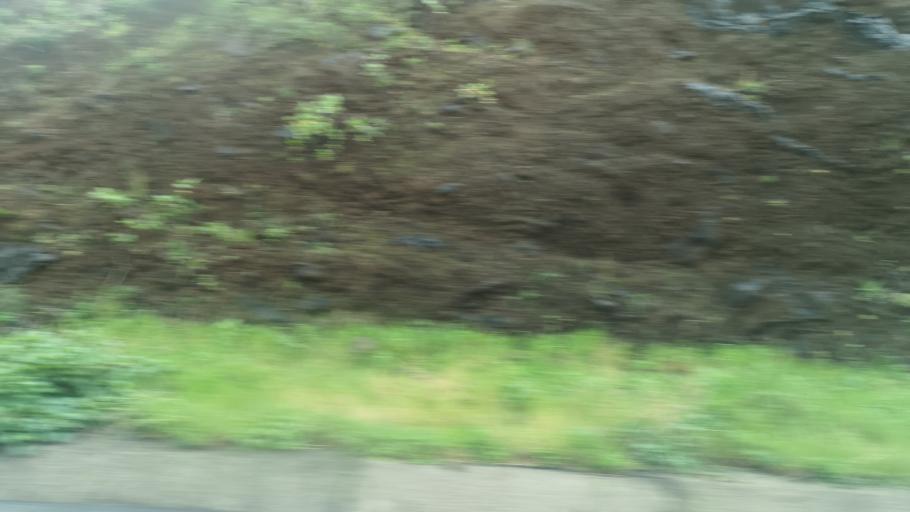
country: ES
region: Canary Islands
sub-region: Provincia de Santa Cruz de Tenerife
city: San Sebastian de la Gomera
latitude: 28.1224
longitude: -17.1533
